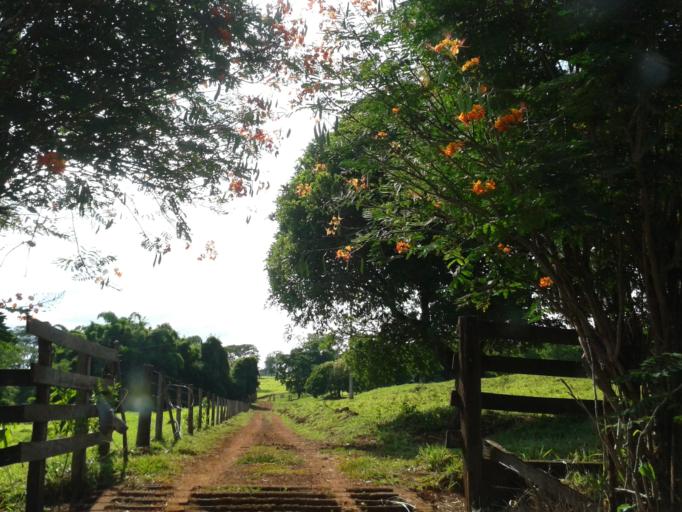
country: BR
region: Minas Gerais
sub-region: Centralina
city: Centralina
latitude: -18.7073
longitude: -49.1980
